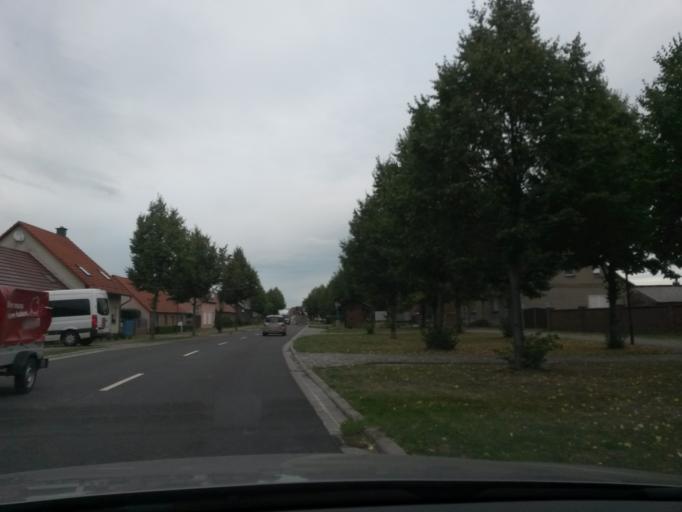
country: DE
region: Saxony-Anhalt
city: Klietz
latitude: 52.6942
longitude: 12.0682
